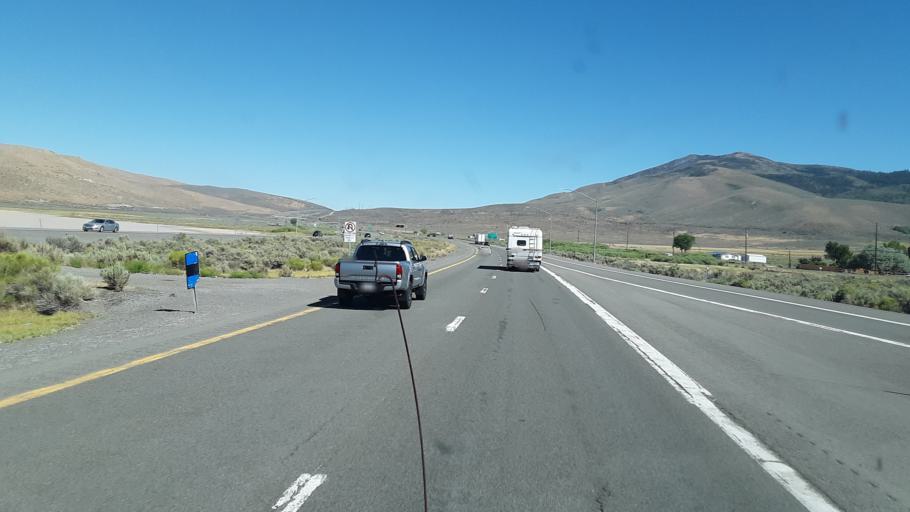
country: US
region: Nevada
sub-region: Washoe County
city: Cold Springs
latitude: 39.6538
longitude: -119.9832
